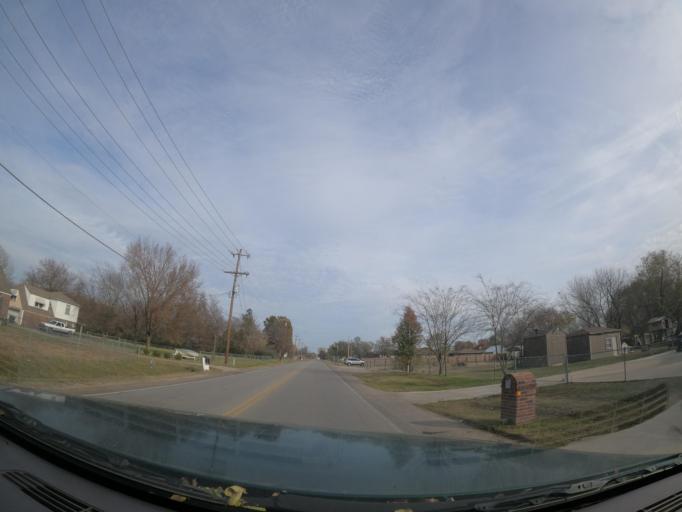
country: US
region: Oklahoma
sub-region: Tulsa County
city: Turley
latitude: 36.2495
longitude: -95.9689
